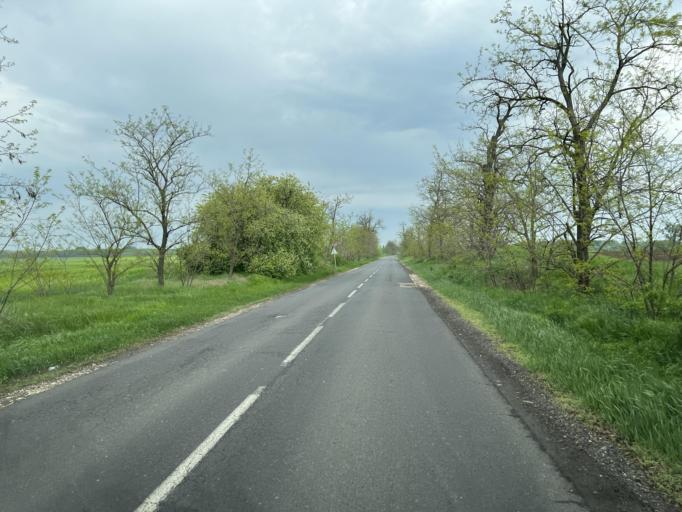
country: HU
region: Pest
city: Tapioszele
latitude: 47.3860
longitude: 19.8916
